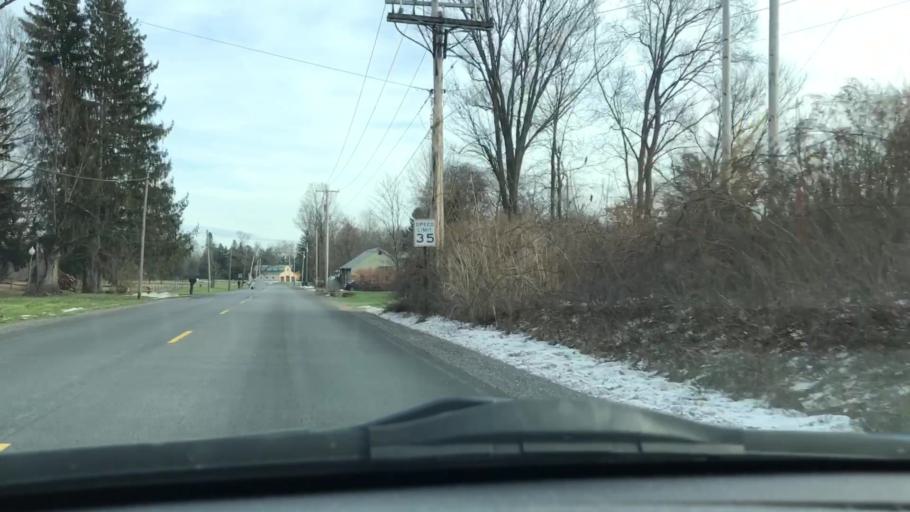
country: US
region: New York
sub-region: Madison County
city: Oneida
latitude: 43.0983
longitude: -75.6328
